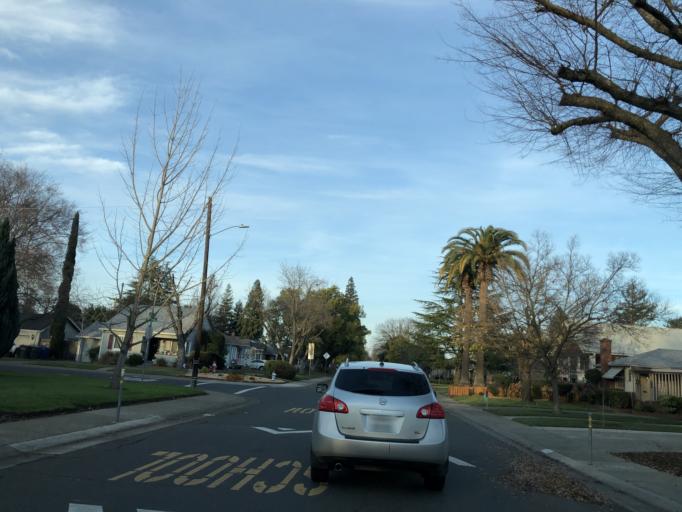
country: US
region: California
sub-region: Sacramento County
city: Sacramento
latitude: 38.5603
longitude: -121.4347
